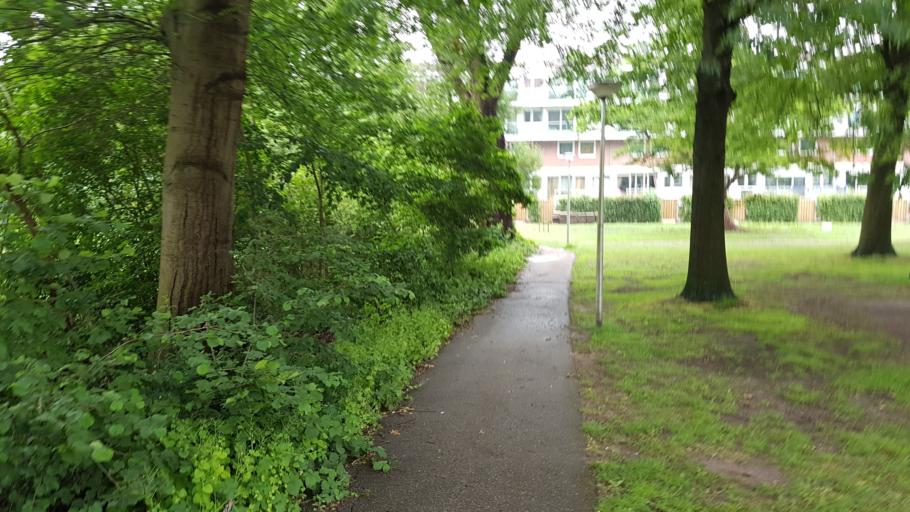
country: NL
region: Overijssel
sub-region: Gemeente Hengelo
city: Hengelo
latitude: 52.2792
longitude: 6.7959
